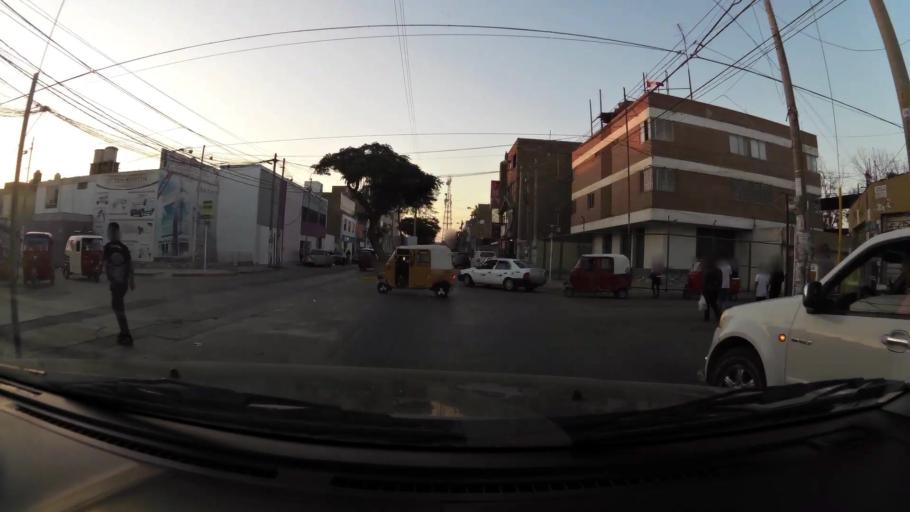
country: PE
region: Ica
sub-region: Provincia de Ica
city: Ica
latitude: -14.0696
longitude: -75.7289
